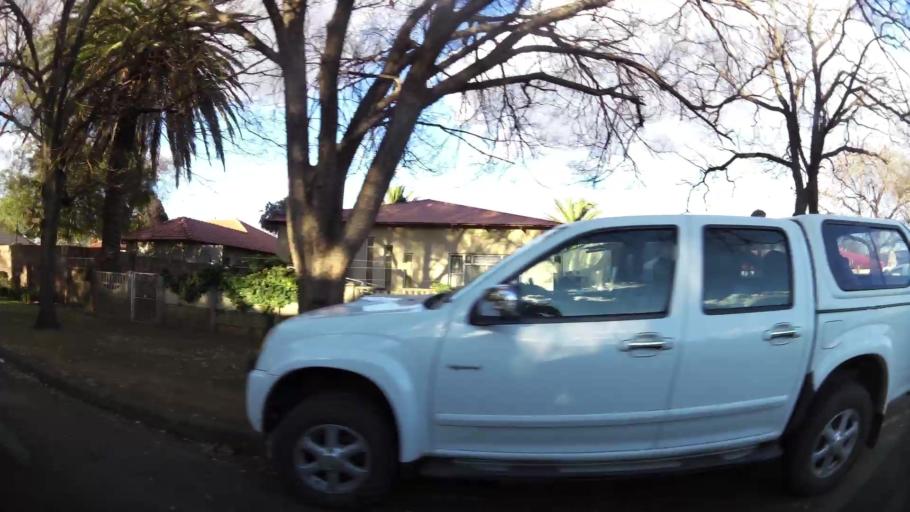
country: ZA
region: North-West
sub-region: Dr Kenneth Kaunda District Municipality
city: Potchefstroom
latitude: -26.7264
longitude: 27.1001
